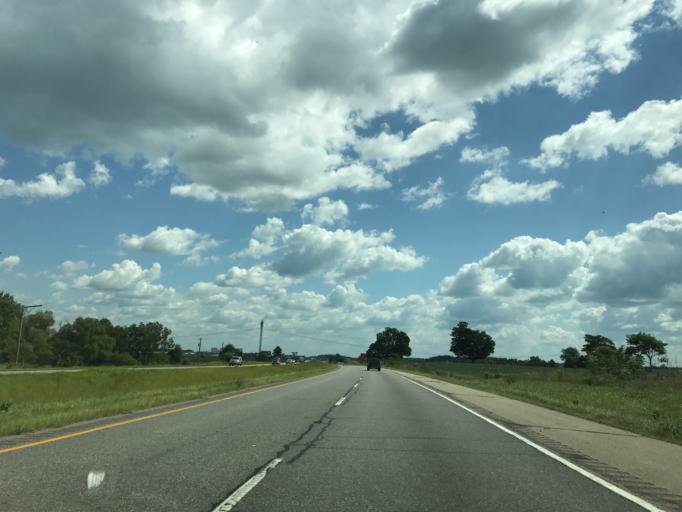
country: US
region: Indiana
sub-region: Marshall County
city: Plymouth
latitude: 41.3613
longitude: -86.3672
